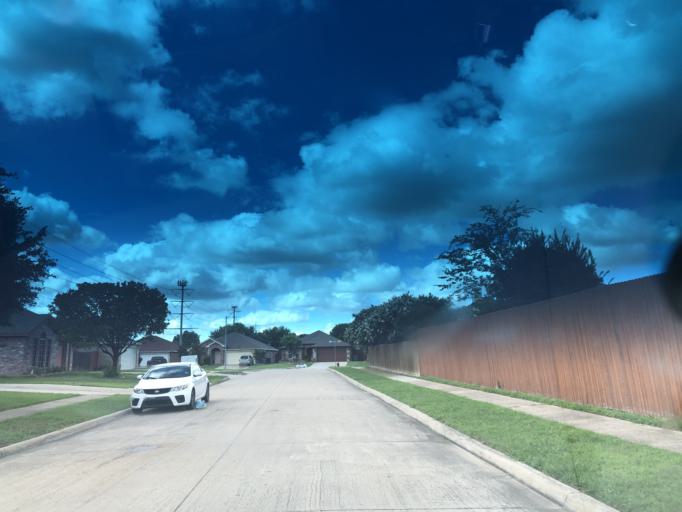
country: US
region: Texas
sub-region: Dallas County
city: Grand Prairie
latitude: 32.6956
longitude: -97.0351
